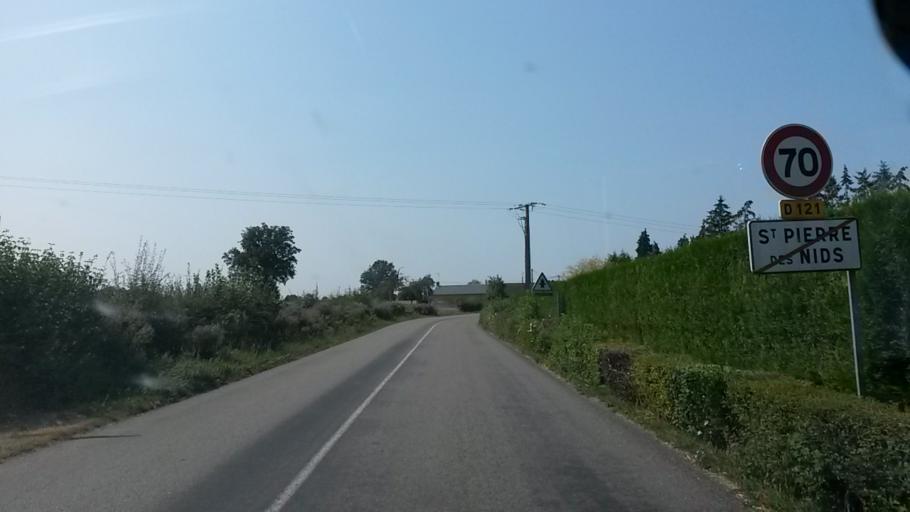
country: FR
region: Pays de la Loire
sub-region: Departement de la Mayenne
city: Saint-Pierre-des-Nids
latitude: 48.3951
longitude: -0.1071
